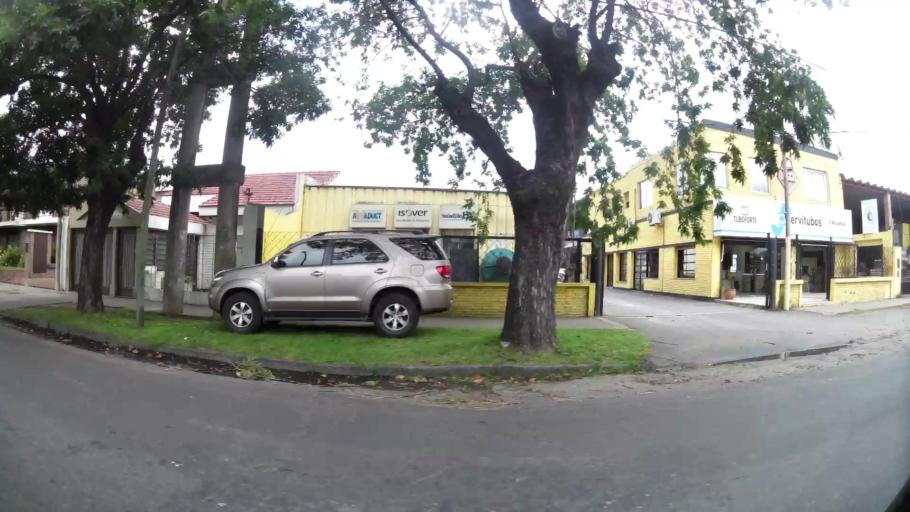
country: AR
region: Santa Fe
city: Gobernador Galvez
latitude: -32.9997
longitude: -60.6413
